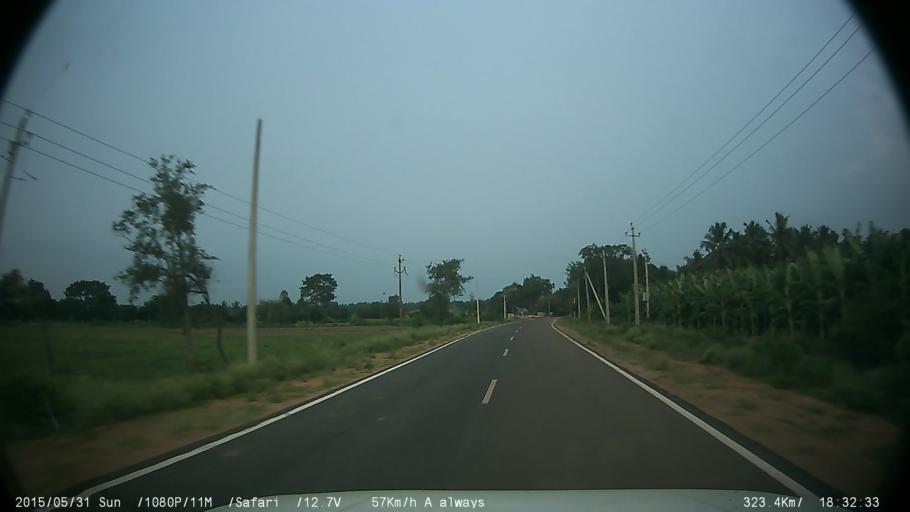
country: IN
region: Karnataka
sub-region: Mysore
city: Nanjangud
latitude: 12.1350
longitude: 76.7477
